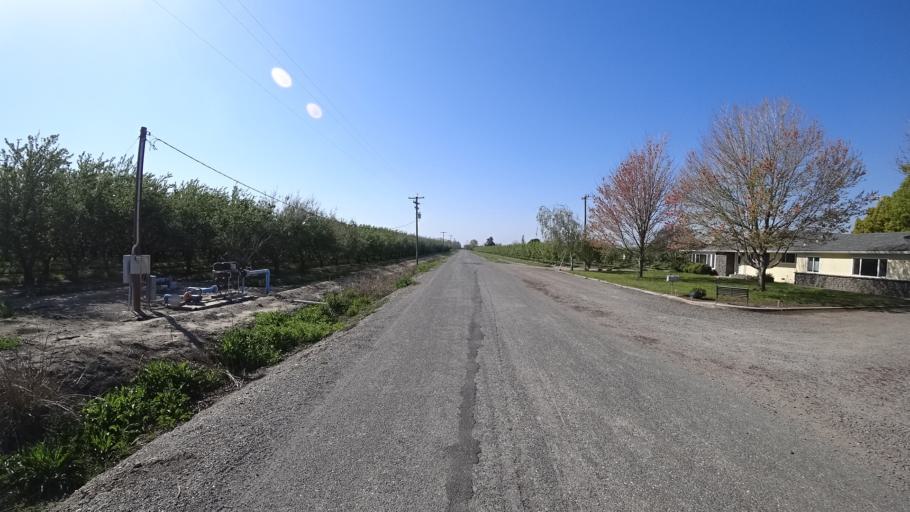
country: US
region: California
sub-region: Glenn County
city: Hamilton City
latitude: 39.6268
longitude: -122.0275
